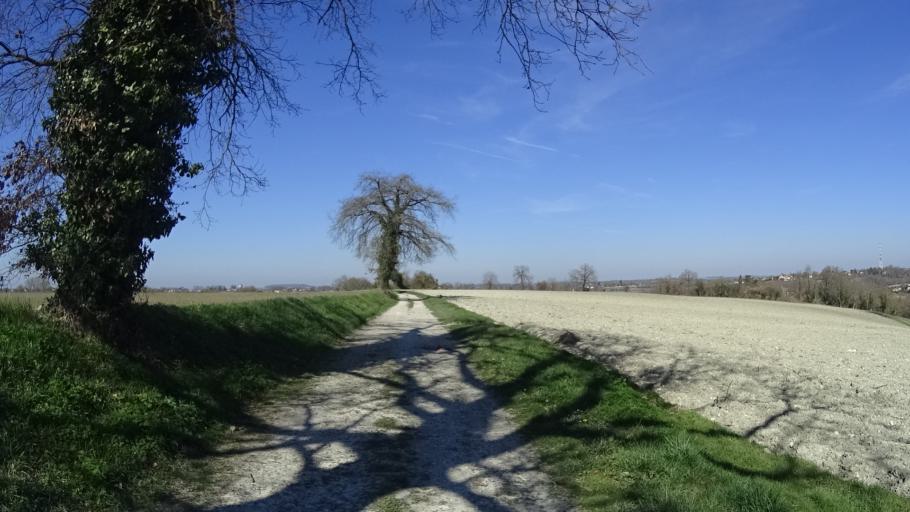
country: FR
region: Aquitaine
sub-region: Departement de la Dordogne
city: Riberac
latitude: 45.2288
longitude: 0.3447
